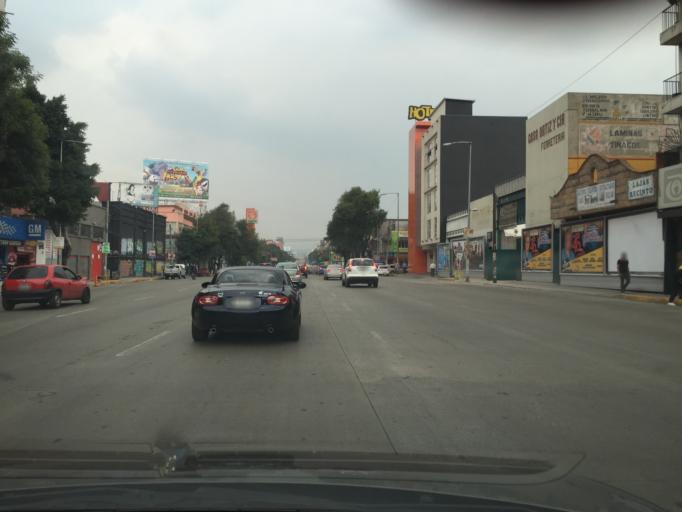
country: MX
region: Mexico City
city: Colonia del Valle
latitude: 19.3830
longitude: -99.1868
